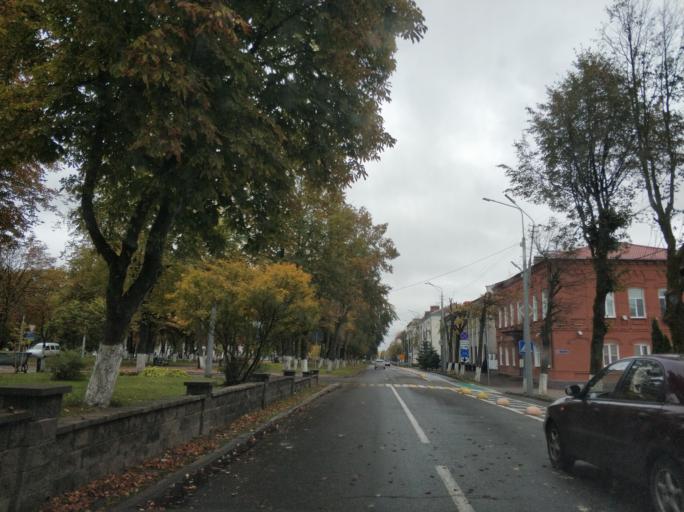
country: BY
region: Vitebsk
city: Polatsk
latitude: 55.4849
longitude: 28.7717
